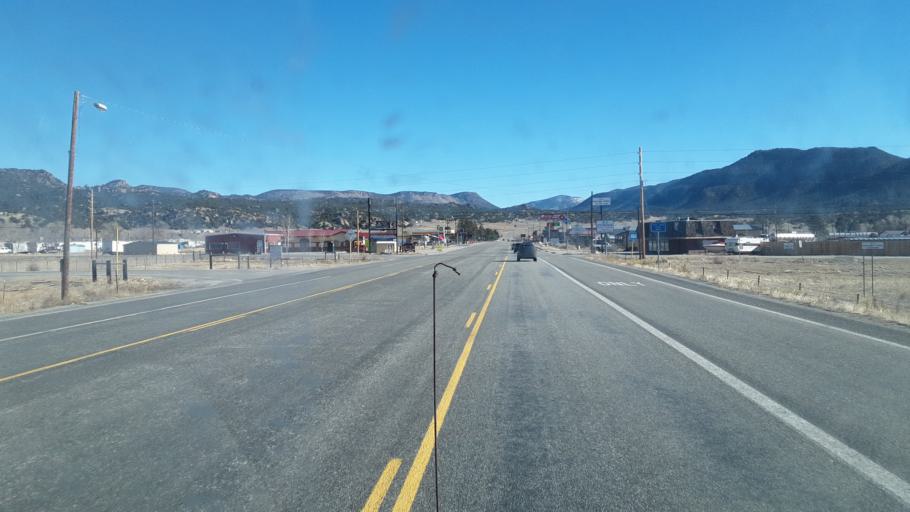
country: US
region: Colorado
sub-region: Chaffee County
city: Buena Vista
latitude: 38.8115
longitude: -106.1099
